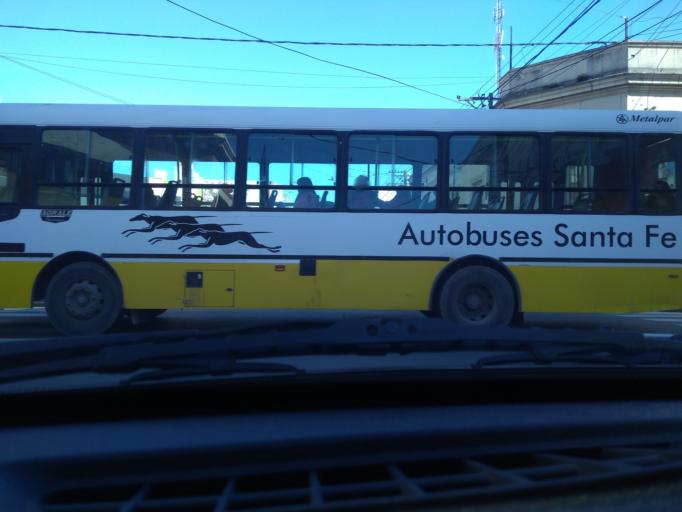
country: AR
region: Santa Fe
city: Santa Fe de la Vera Cruz
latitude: -31.6512
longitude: -60.7092
